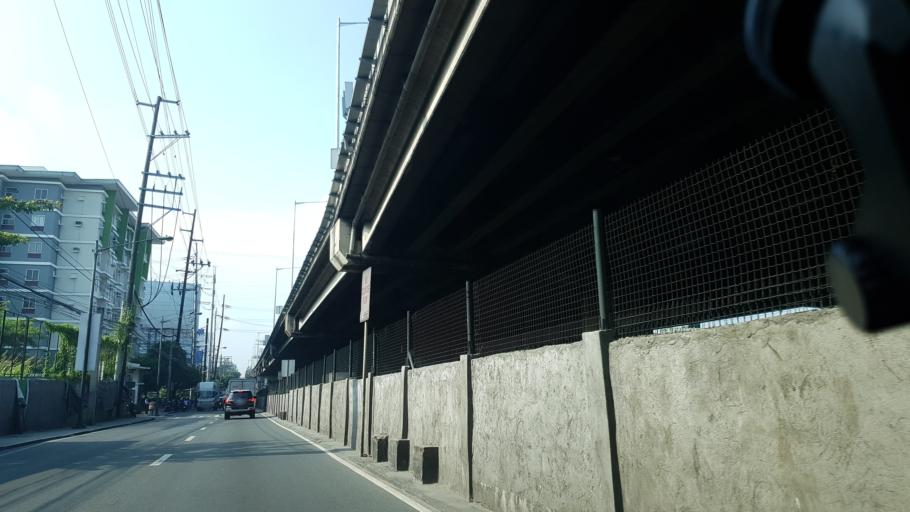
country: PH
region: Calabarzon
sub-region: Province of Rizal
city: Taguig
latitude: 14.4927
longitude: 121.0422
